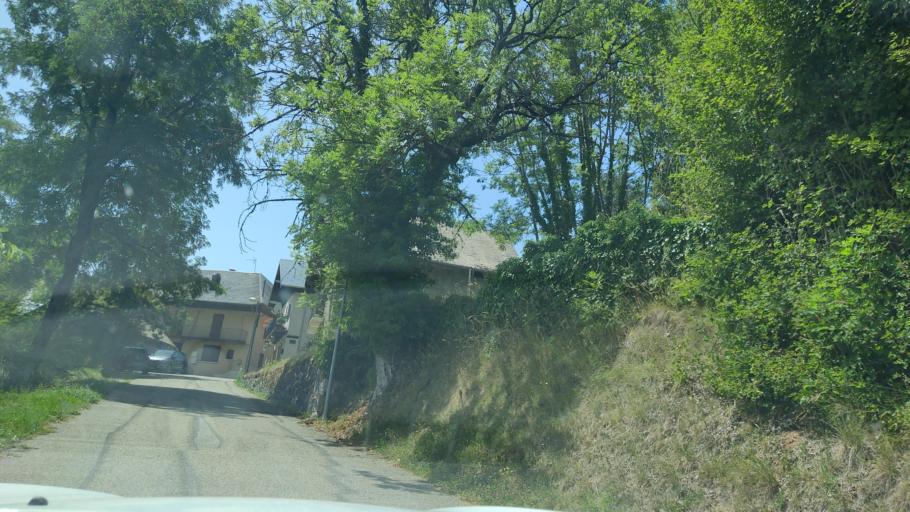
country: FR
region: Rhone-Alpes
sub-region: Departement de la Savoie
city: Coise-Saint-Jean-Pied-Gauthier
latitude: 45.5735
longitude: 6.1419
